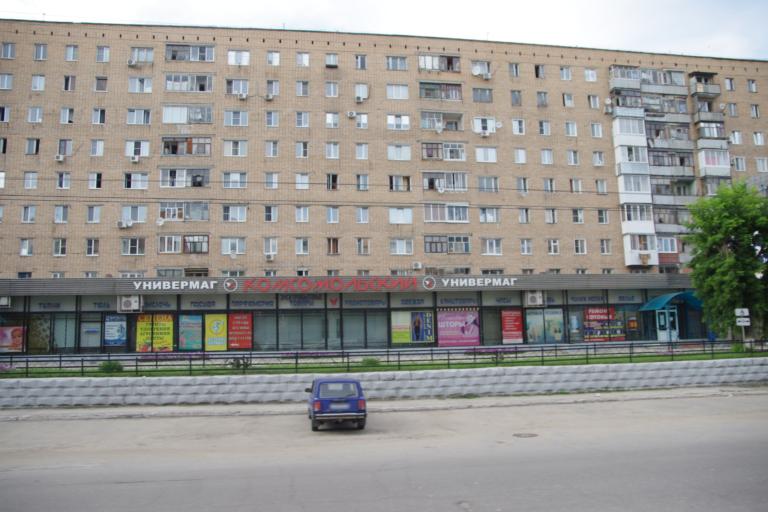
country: RU
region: Samara
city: Zhigulevsk
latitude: 53.4814
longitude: 49.4833
